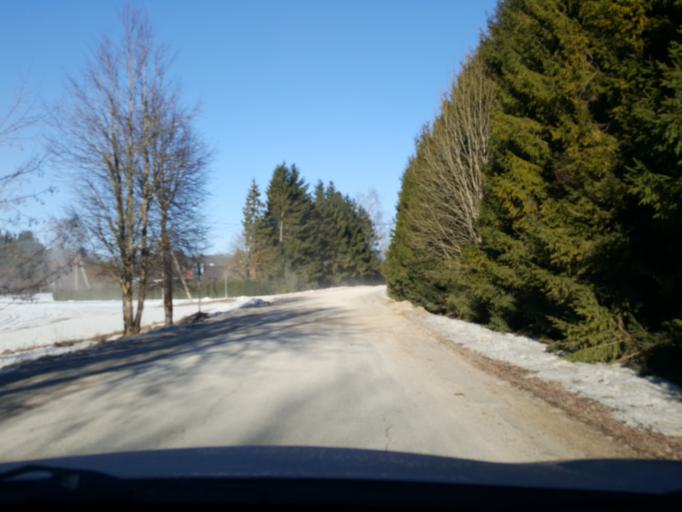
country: EE
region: Viljandimaa
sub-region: Viljandi linn
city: Viljandi
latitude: 58.4251
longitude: 25.5334
